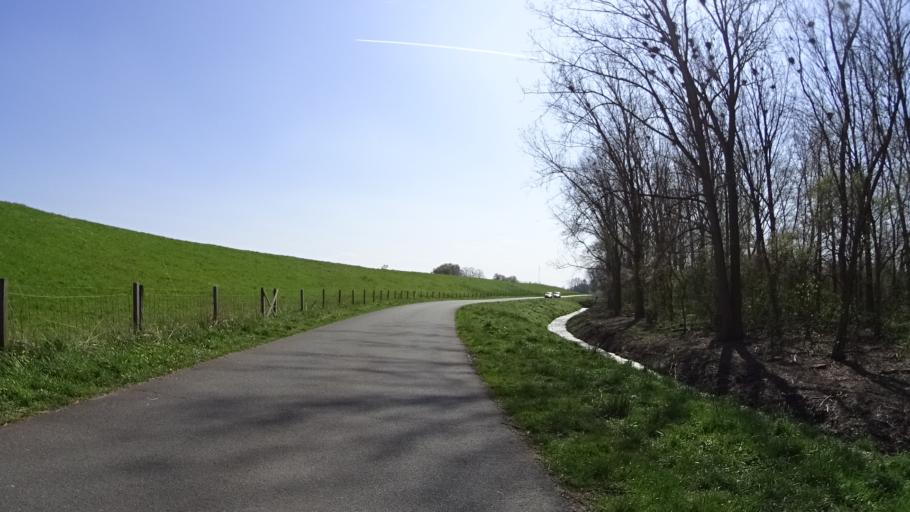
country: DE
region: Lower Saxony
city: Weener
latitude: 53.1669
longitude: 7.3679
